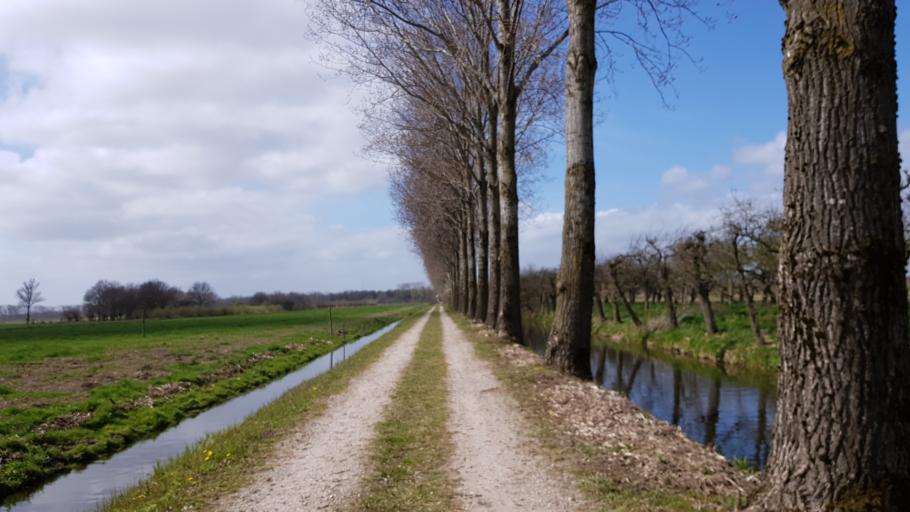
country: NL
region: Utrecht
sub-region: Gemeente IJsselstein
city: IJsselstein
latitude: 51.9587
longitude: 5.0244
